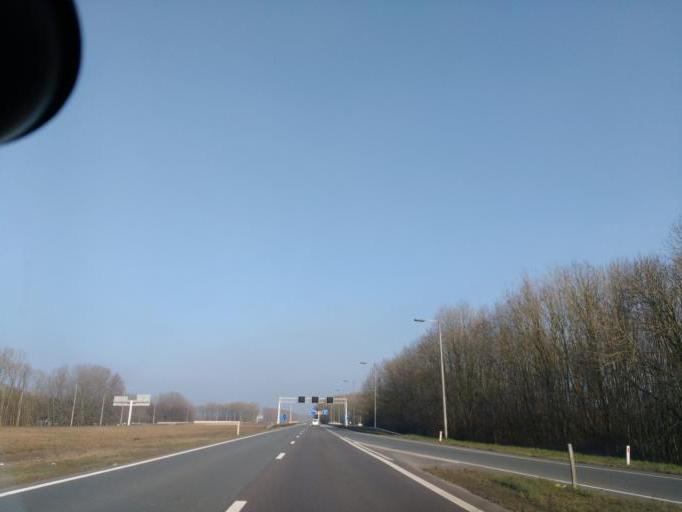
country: NL
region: Gelderland
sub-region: Gemeente Overbetuwe
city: Elst
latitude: 51.8959
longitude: 5.8632
